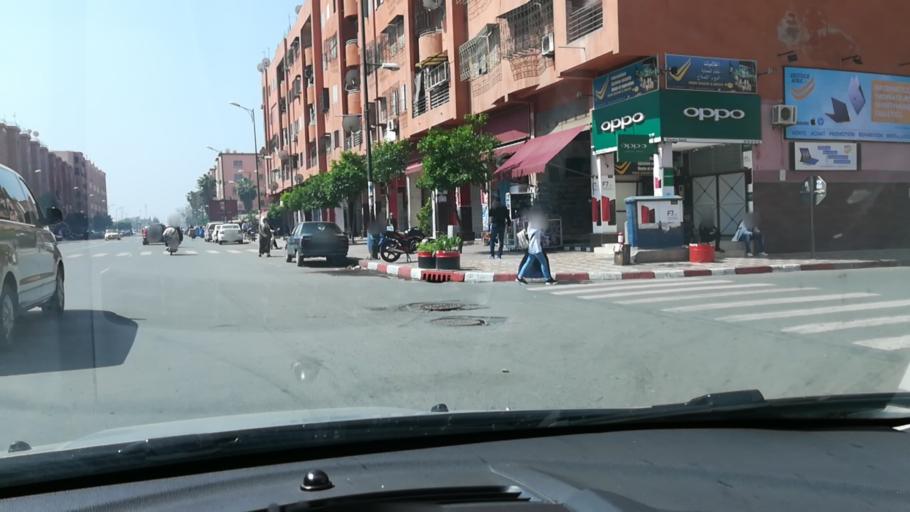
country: MA
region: Marrakech-Tensift-Al Haouz
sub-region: Marrakech
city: Marrakesh
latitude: 31.6315
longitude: -8.0585
